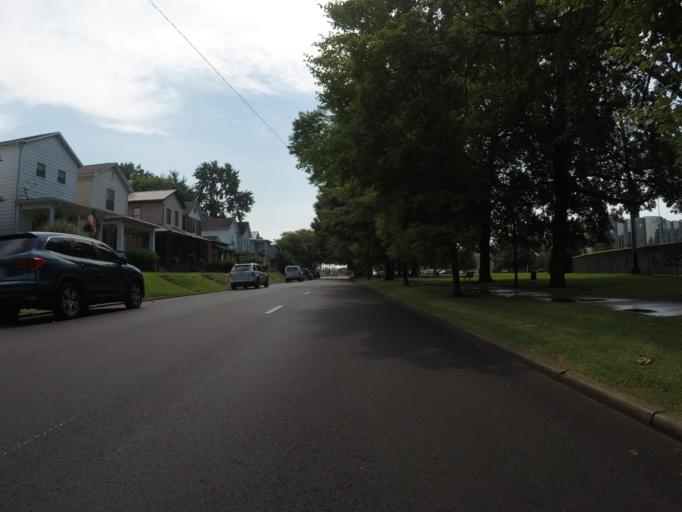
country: US
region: Kentucky
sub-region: Boyd County
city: Ashland
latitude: 38.4738
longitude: -82.6351
